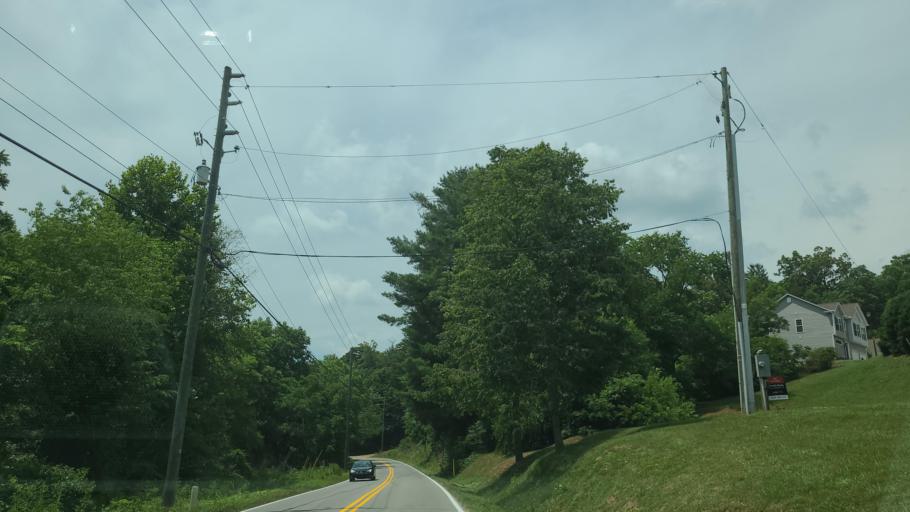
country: US
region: North Carolina
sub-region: Buncombe County
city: Avery Creek
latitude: 35.4884
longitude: -82.5736
